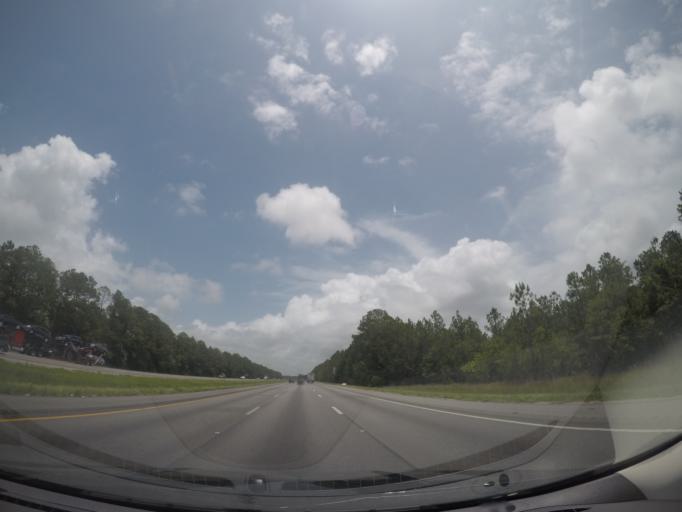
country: US
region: Mississippi
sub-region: Jackson County
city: Gulf Hills
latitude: 30.4542
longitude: -88.8217
